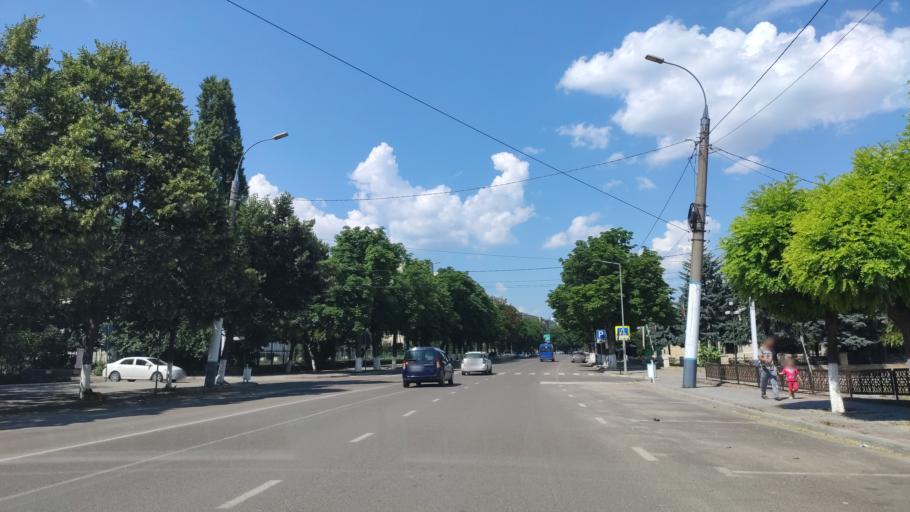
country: MD
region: Raionul Soroca
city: Soroca
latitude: 48.1581
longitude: 28.3022
